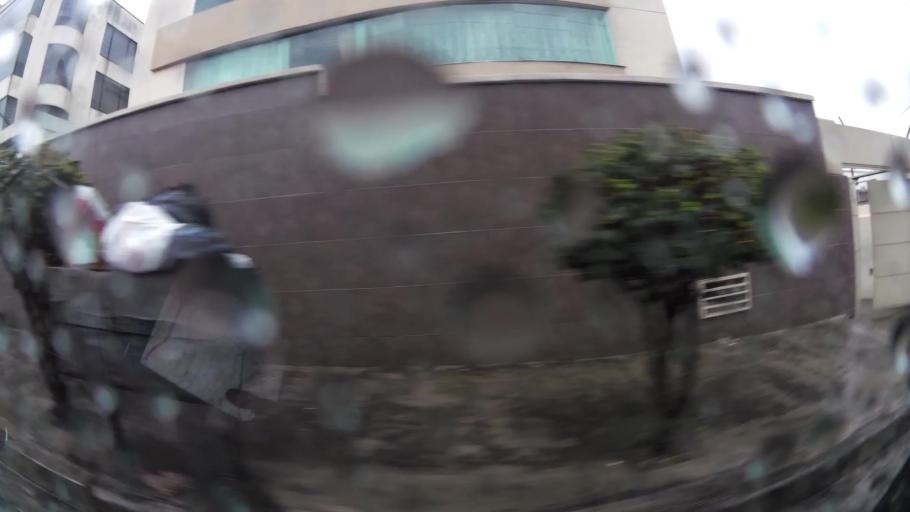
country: EC
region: Pichincha
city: Quito
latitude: -0.1571
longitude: -78.4608
